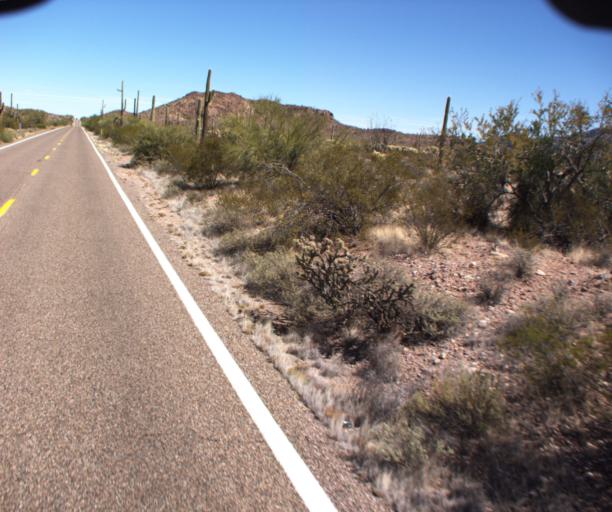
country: MX
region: Sonora
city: Sonoyta
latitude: 32.0752
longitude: -112.7813
